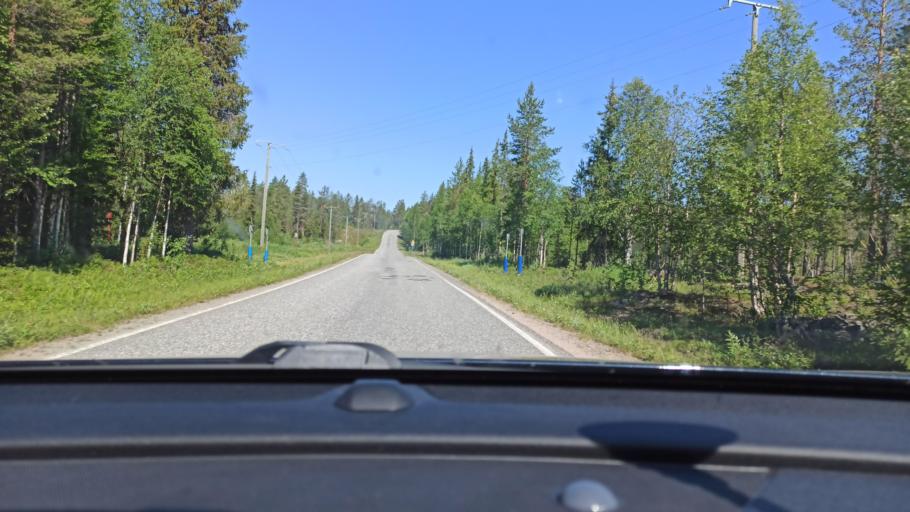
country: FI
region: Lapland
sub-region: Tunturi-Lappi
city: Kolari
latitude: 67.6341
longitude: 24.1598
